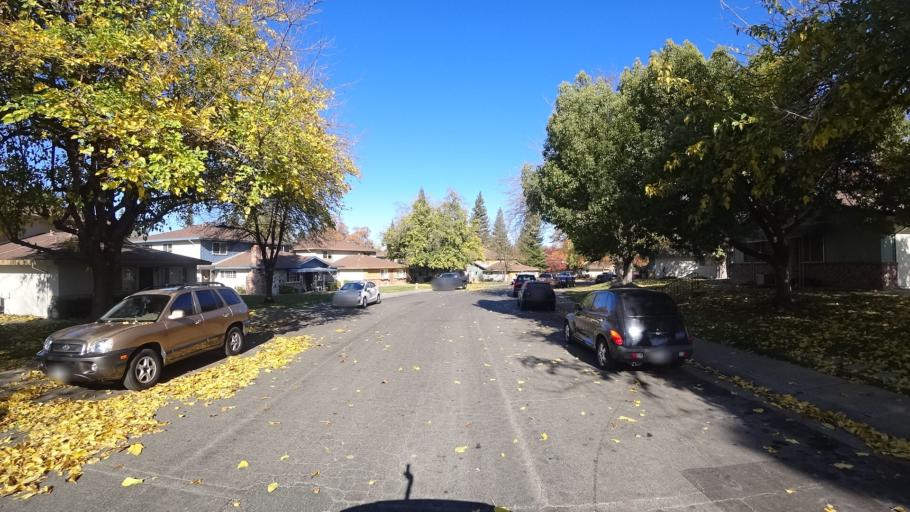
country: US
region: California
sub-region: Sacramento County
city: Antelope
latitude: 38.6810
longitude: -121.3152
